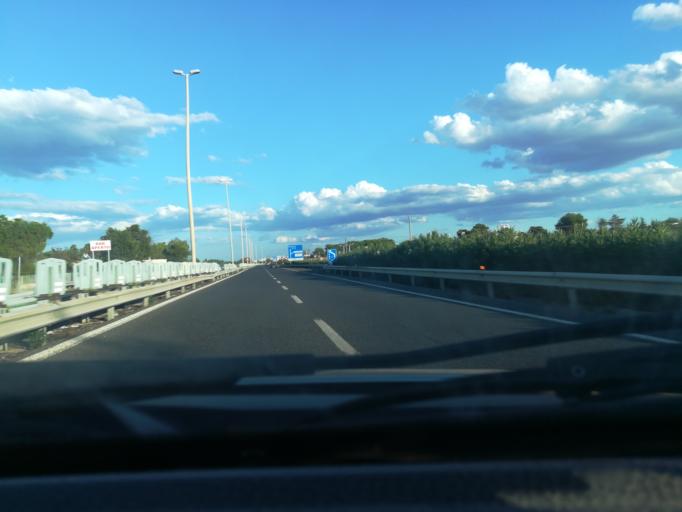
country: IT
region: Apulia
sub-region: Provincia di Bari
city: Mola di Bari
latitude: 41.0737
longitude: 17.0578
